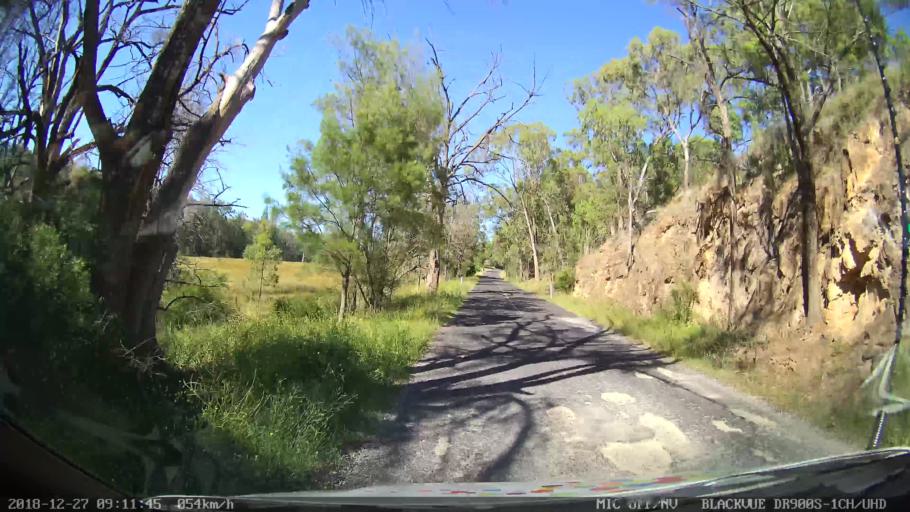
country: AU
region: New South Wales
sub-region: Lithgow
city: Portland
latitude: -33.1374
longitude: 150.1117
